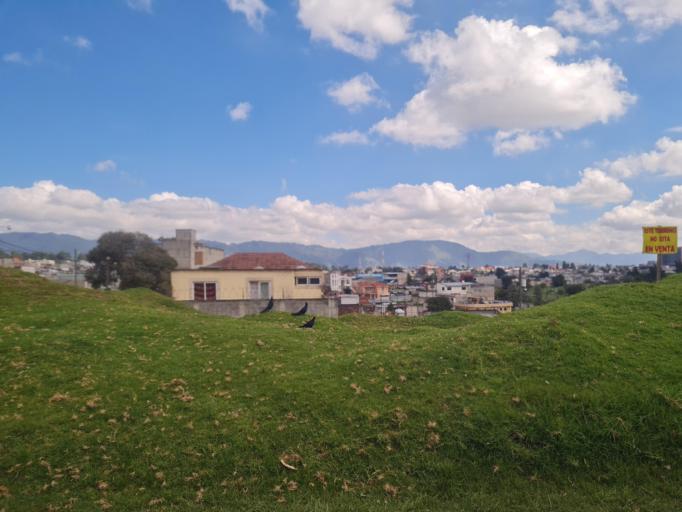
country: GT
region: Quetzaltenango
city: Quetzaltenango
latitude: 14.8354
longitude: -91.5332
